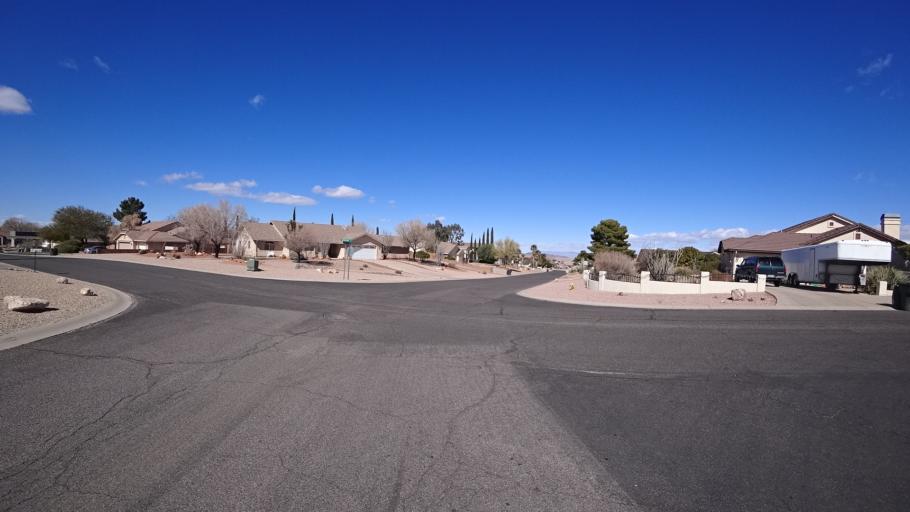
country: US
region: Arizona
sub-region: Mohave County
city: Kingman
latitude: 35.1975
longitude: -113.9660
